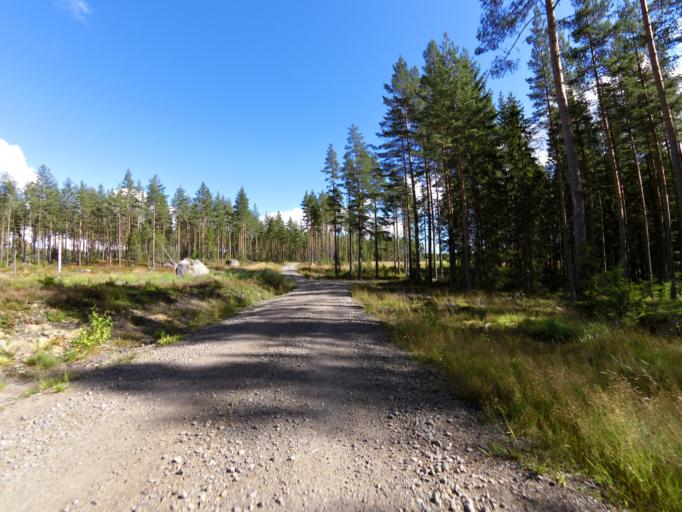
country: SE
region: Gaevleborg
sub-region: Ockelbo Kommun
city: Ockelbo
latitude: 60.8263
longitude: 16.7552
